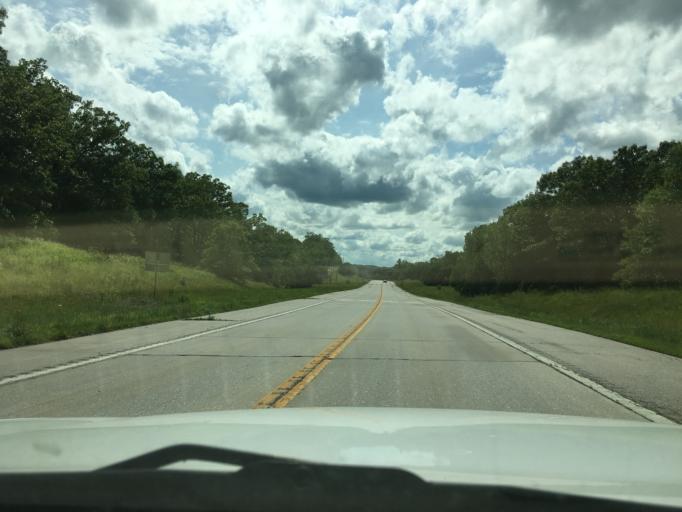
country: US
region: Missouri
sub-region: Franklin County
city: Gerald
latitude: 38.4236
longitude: -91.2637
